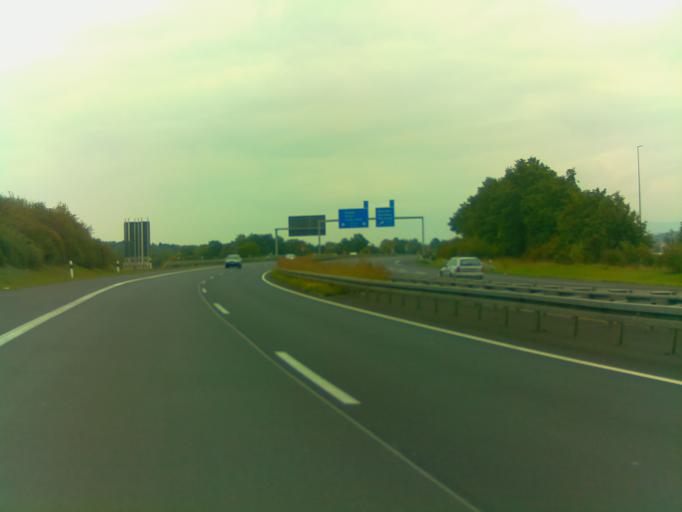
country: DE
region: Hesse
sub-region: Regierungsbezirk Kassel
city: Eichenzell
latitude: 50.4900
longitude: 9.7073
